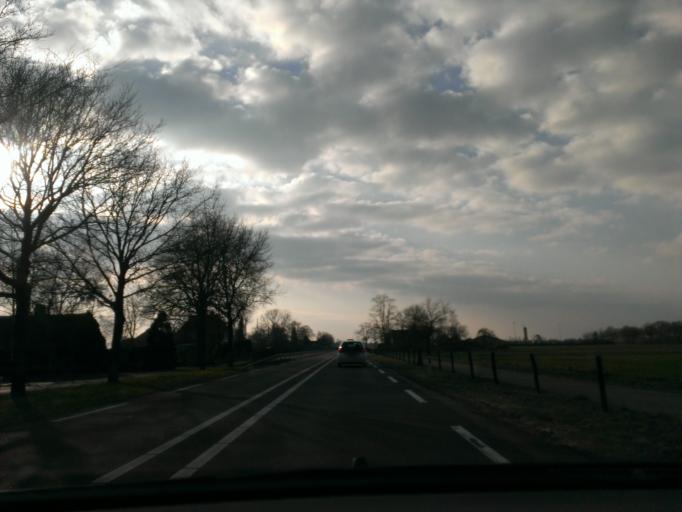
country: NL
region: Overijssel
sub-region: Gemeente Wierden
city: Wierden
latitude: 52.3594
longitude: 6.5549
